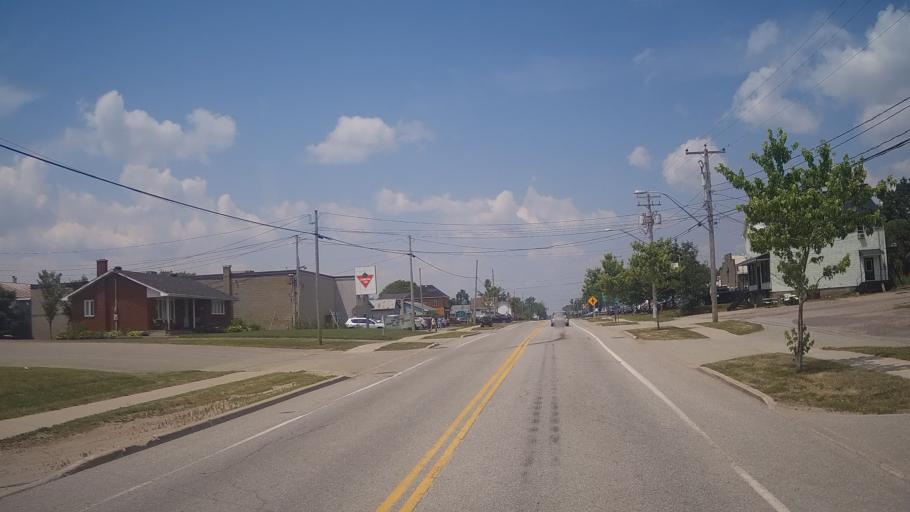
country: CA
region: Quebec
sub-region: Outaouais
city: Shawville
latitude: 45.5986
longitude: -76.4908
